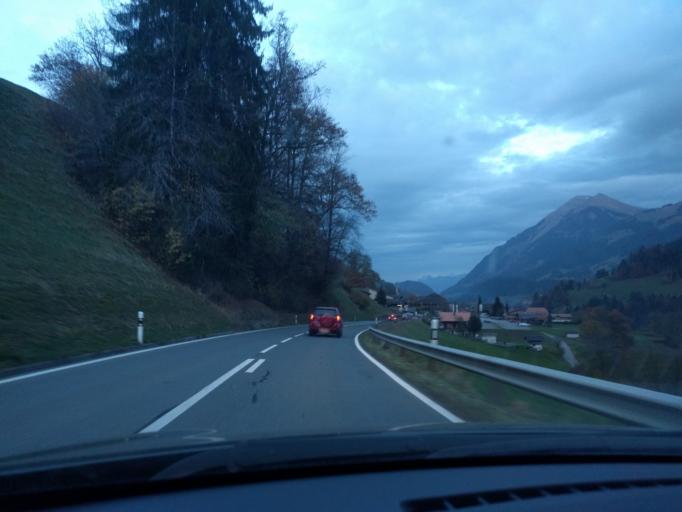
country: CH
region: Bern
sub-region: Frutigen-Niedersimmental District
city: Erlenbach im Simmental
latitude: 46.6597
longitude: 7.5412
